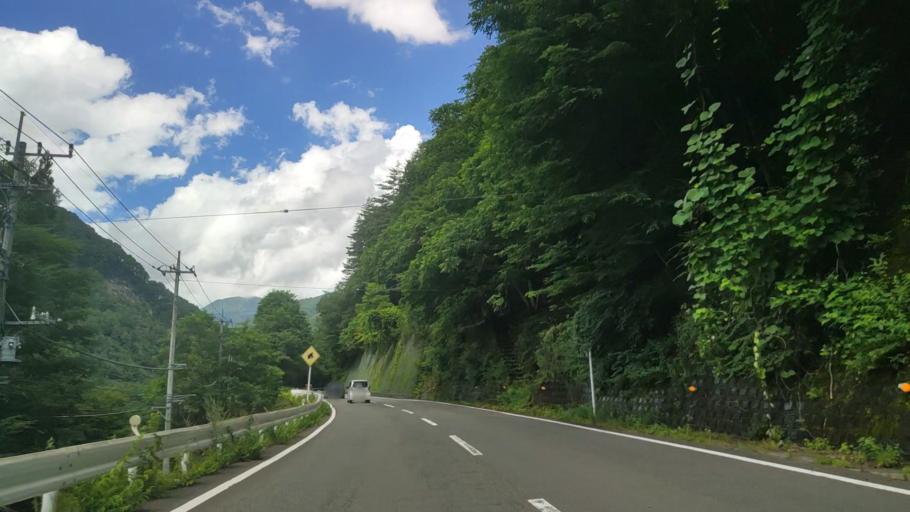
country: JP
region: Yamanashi
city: Enzan
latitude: 35.8201
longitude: 138.7585
